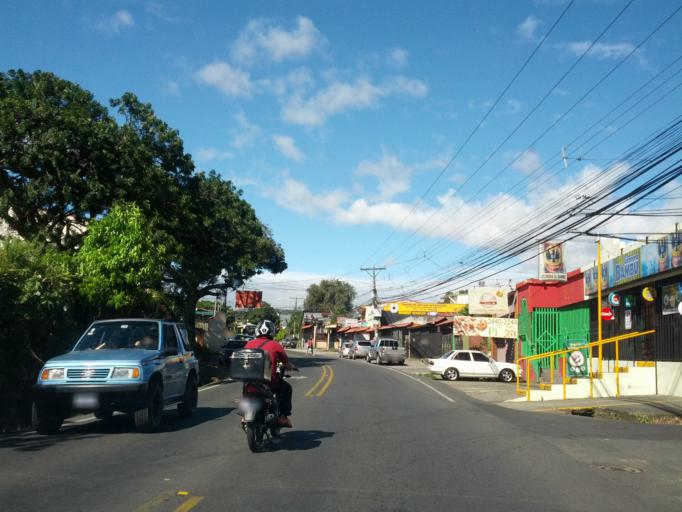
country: CR
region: Alajuela
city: Alajuela
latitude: 10.0233
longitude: -84.2066
